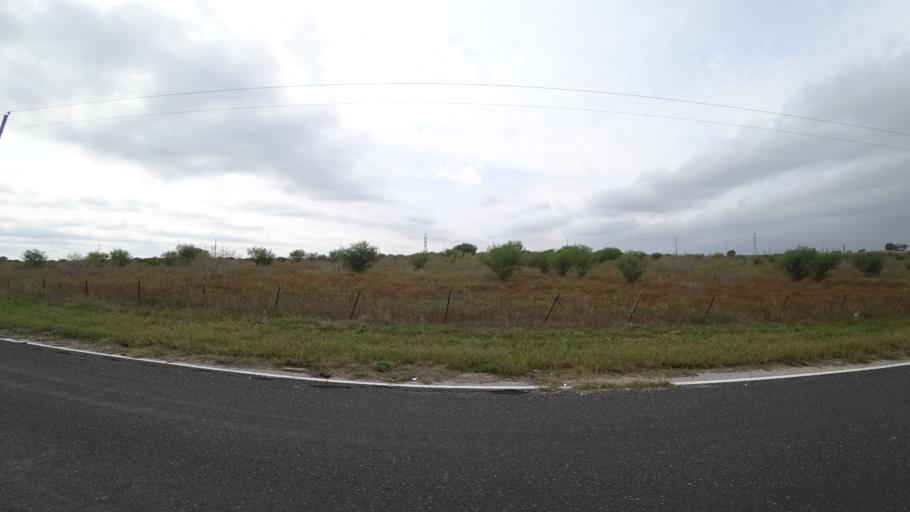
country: US
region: Texas
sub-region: Travis County
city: Manor
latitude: 30.3728
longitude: -97.5718
